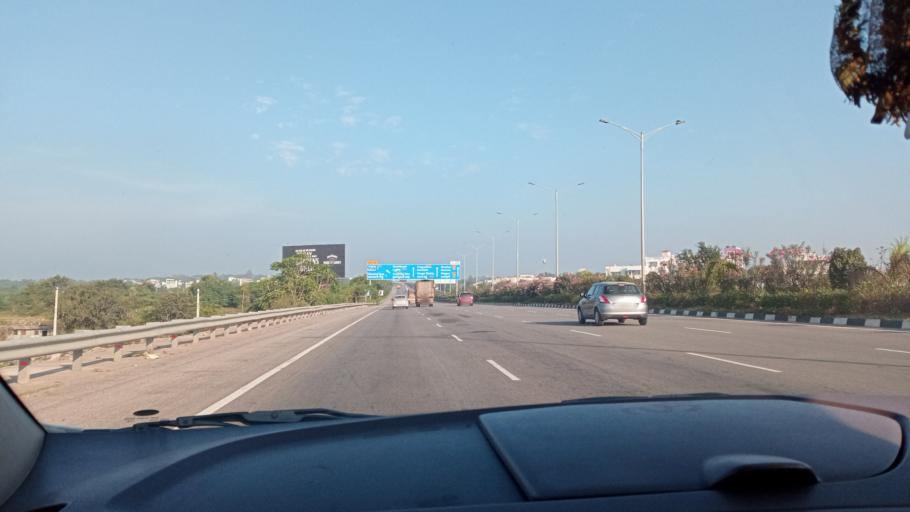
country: IN
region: Telangana
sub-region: Hyderabad
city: Hyderabad
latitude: 17.3297
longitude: 78.3718
